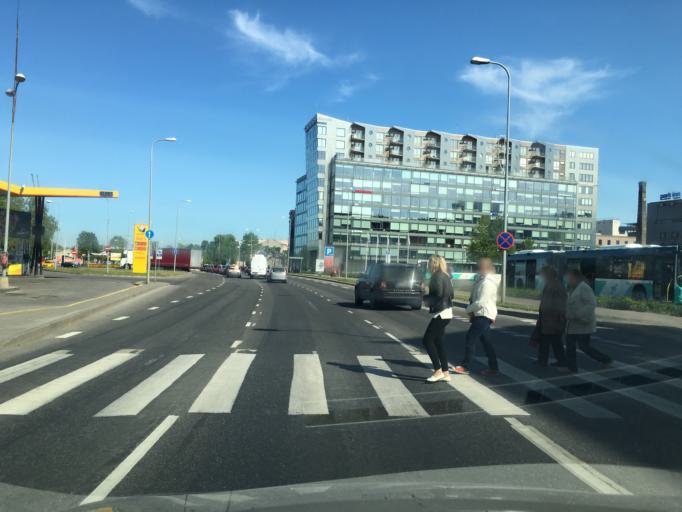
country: EE
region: Harju
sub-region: Tallinna linn
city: Tallinn
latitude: 59.4396
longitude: 24.7587
